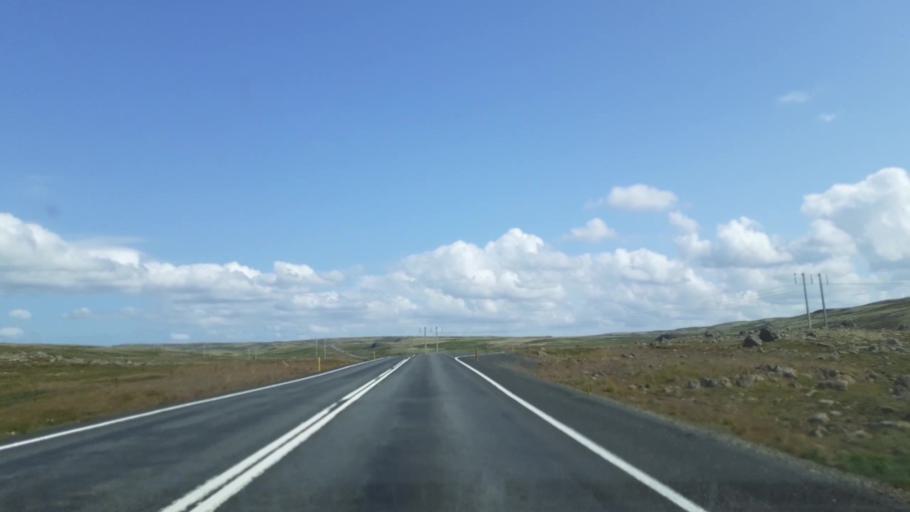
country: IS
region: West
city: Borgarnes
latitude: 64.9290
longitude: -21.0955
